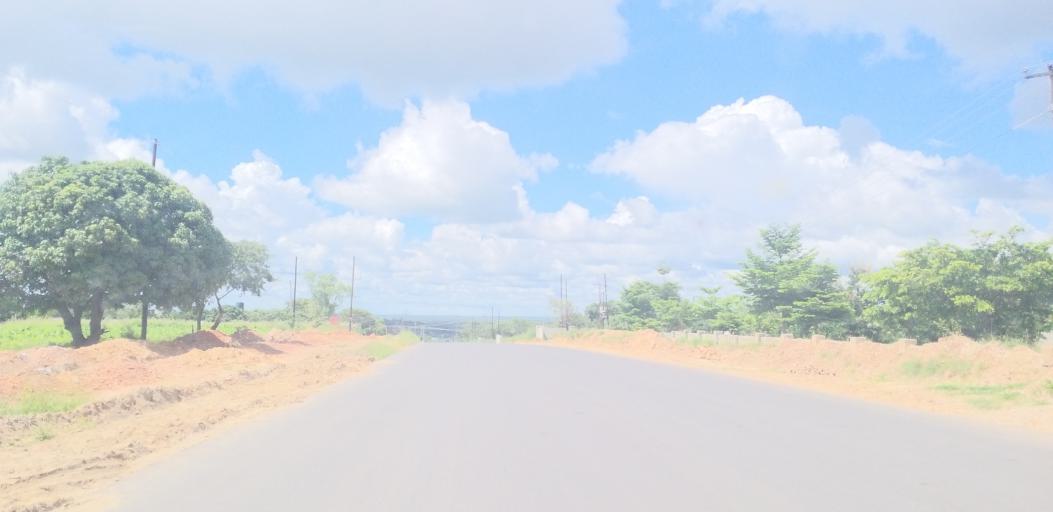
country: ZM
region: Lusaka
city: Lusaka
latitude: -15.3505
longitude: 28.3256
